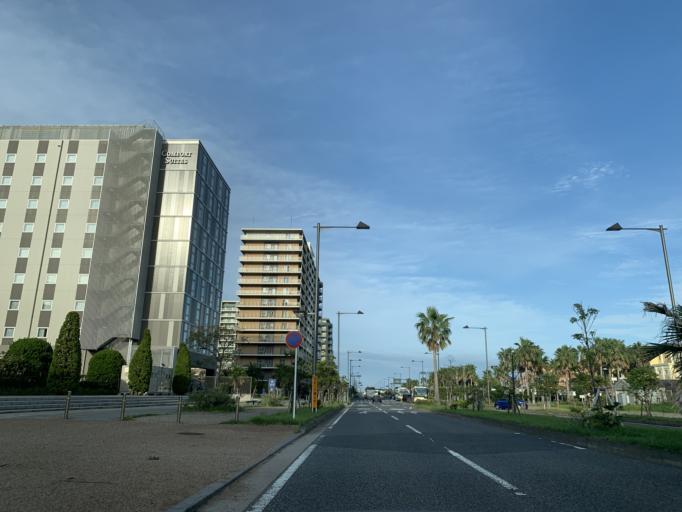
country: JP
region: Tokyo
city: Urayasu
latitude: 35.6376
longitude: 139.9272
